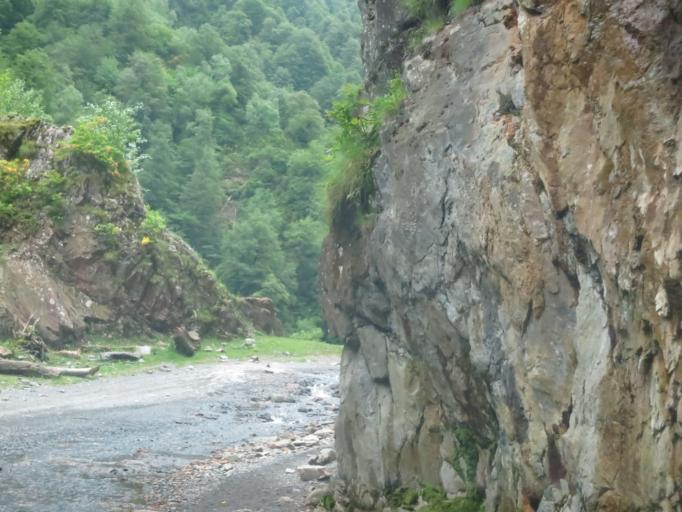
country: GE
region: Kakheti
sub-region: Telavi
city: Telavi
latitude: 42.2363
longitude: 45.4916
